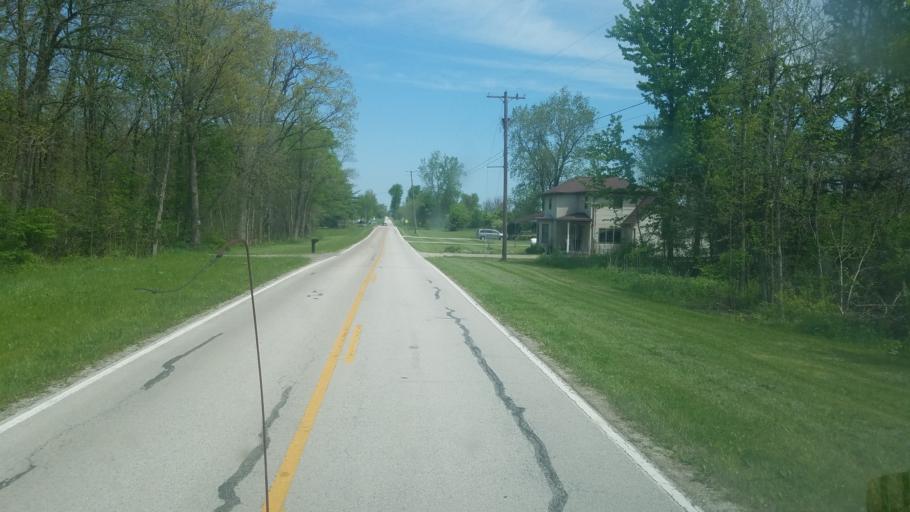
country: US
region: Ohio
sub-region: Sandusky County
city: Stony Prairie
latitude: 41.4030
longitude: -83.2023
